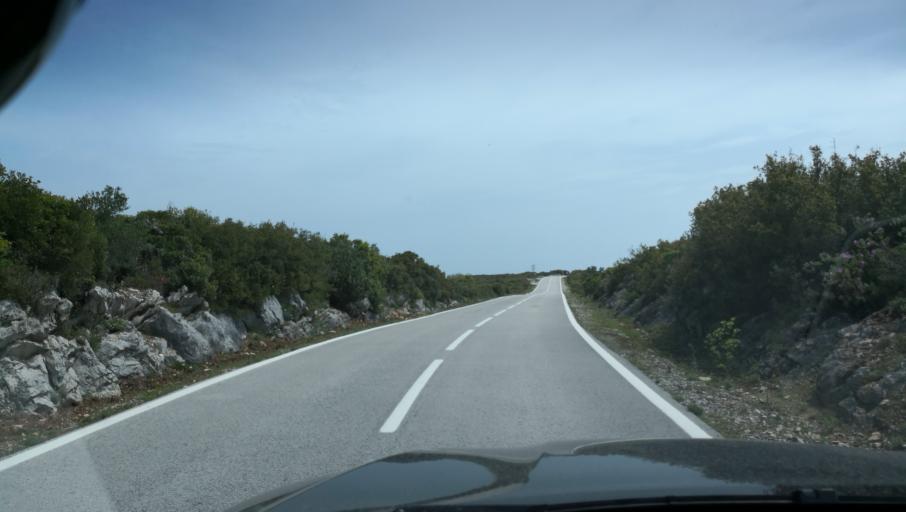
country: PT
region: Setubal
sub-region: Palmela
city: Quinta do Anjo
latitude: 38.4941
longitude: -8.9663
